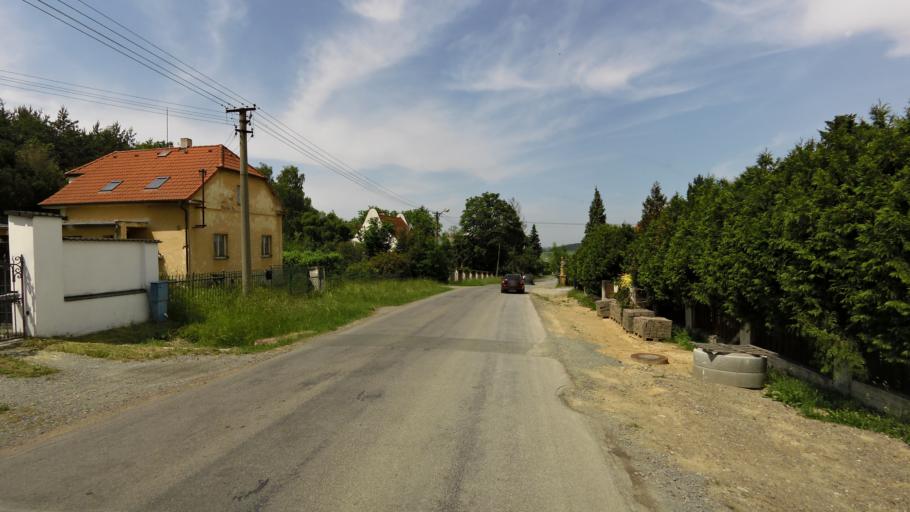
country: CZ
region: Plzensky
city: Stary Plzenec
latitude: 49.6877
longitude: 13.4758
